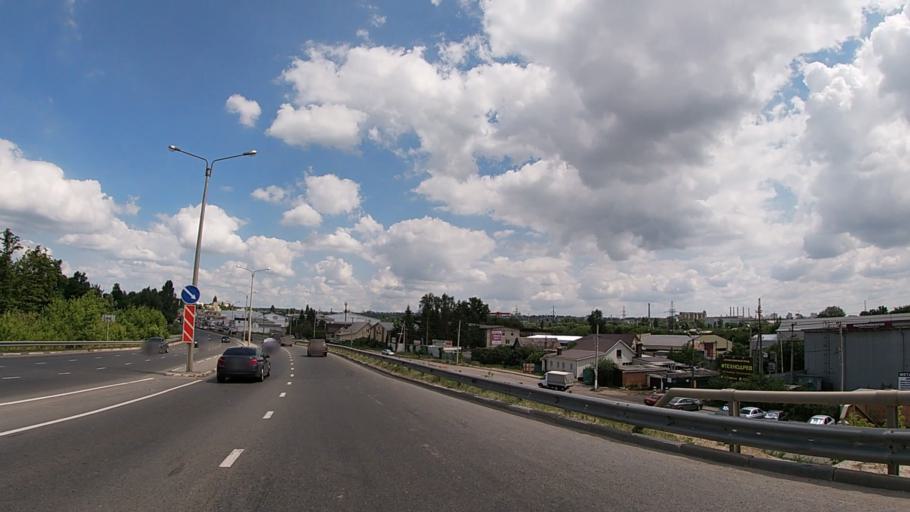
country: RU
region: Belgorod
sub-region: Belgorodskiy Rayon
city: Belgorod
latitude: 50.6081
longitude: 36.5331
